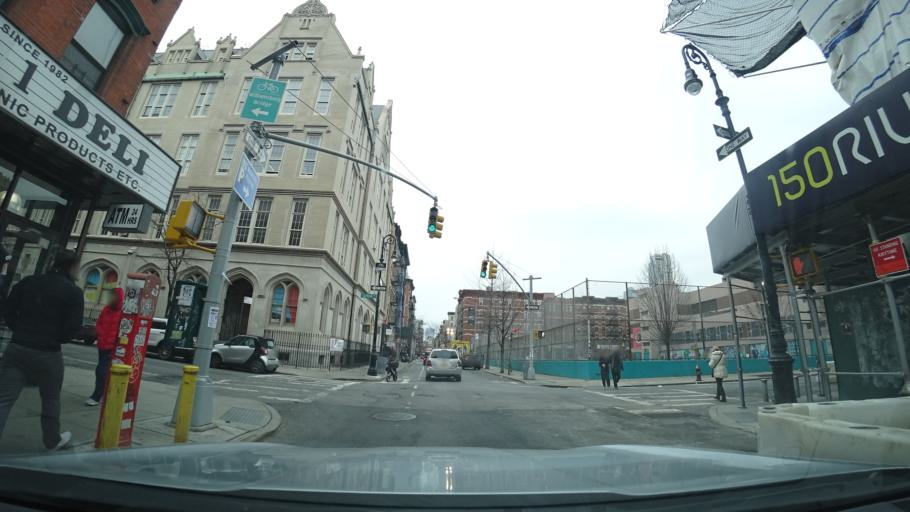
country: US
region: New York
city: New York City
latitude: 40.7192
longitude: -73.9858
